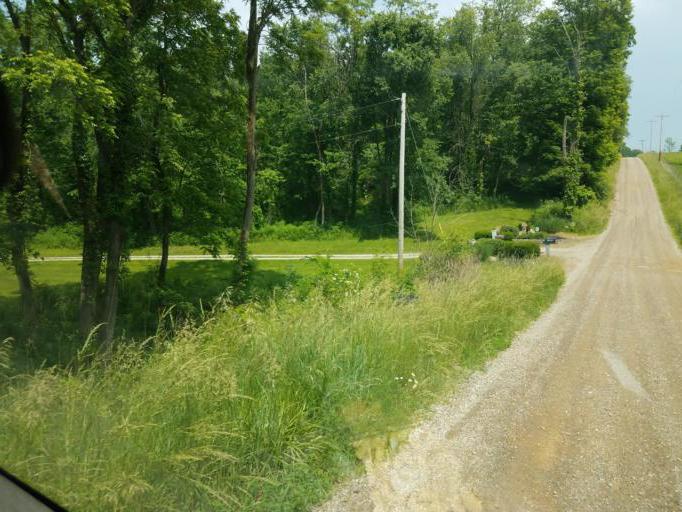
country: US
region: Ohio
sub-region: Knox County
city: Oak Hill
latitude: 40.3567
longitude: -82.2706
